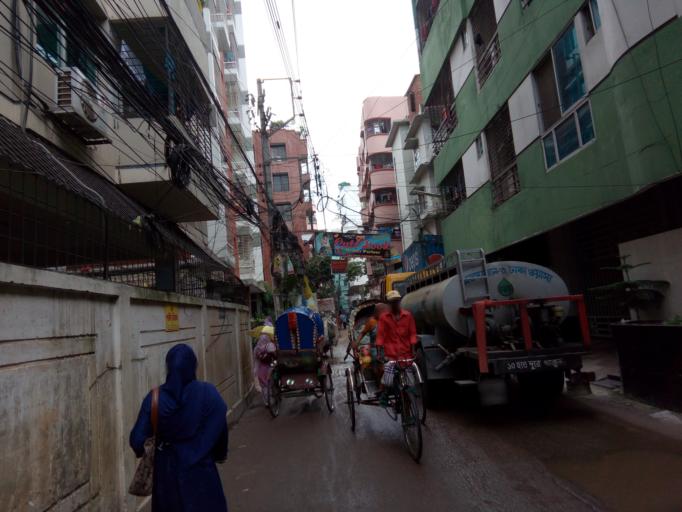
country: BD
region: Dhaka
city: Azimpur
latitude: 23.7504
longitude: 90.3817
